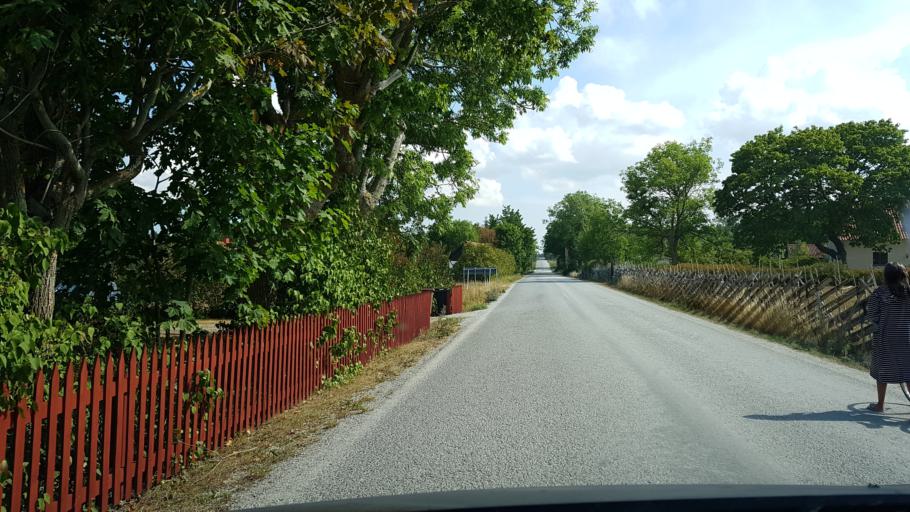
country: SE
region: Gotland
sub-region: Gotland
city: Visby
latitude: 57.8243
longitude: 18.5145
